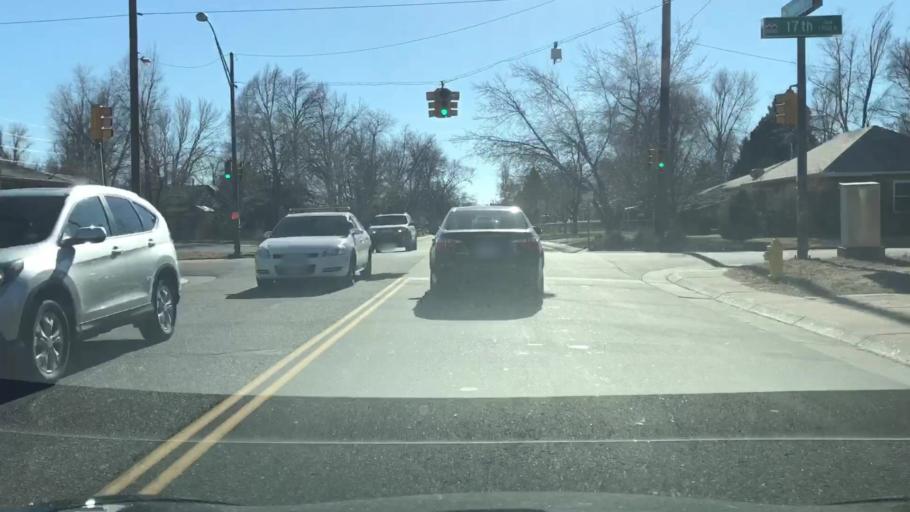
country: US
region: Colorado
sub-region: Adams County
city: Aurora
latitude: 39.7442
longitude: -104.8847
